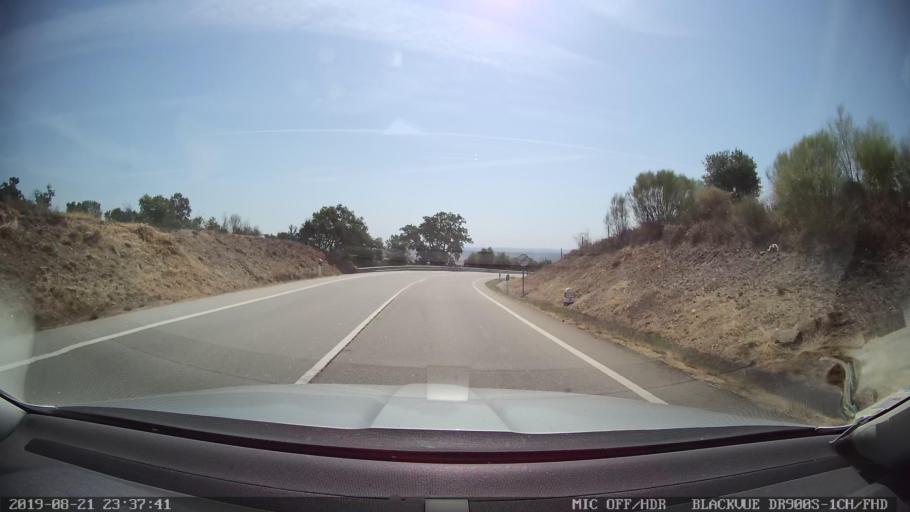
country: PT
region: Guarda
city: Alcains
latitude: 39.8666
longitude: -7.3571
